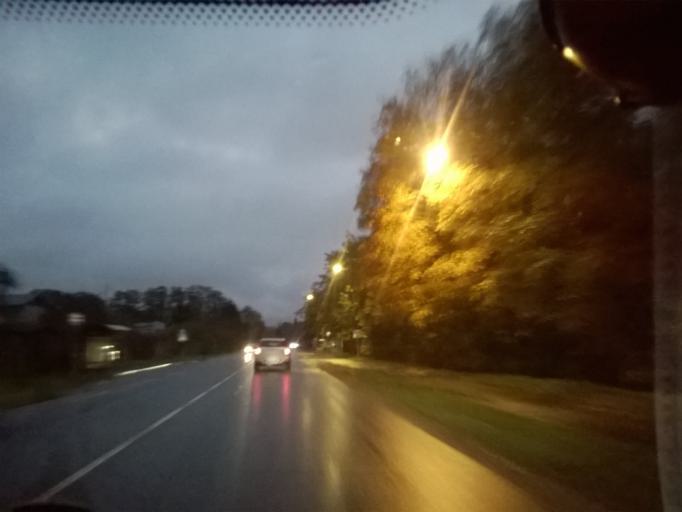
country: EE
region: Harju
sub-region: Viimsi vald
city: Haabneeme
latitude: 59.5165
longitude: 24.8137
